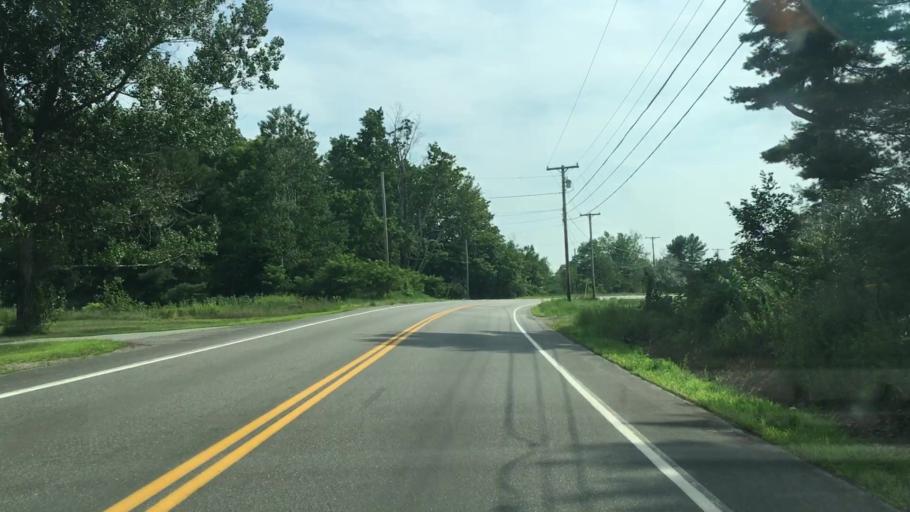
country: US
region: Maine
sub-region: Kennebec County
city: Windsor
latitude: 44.2935
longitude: -69.5855
